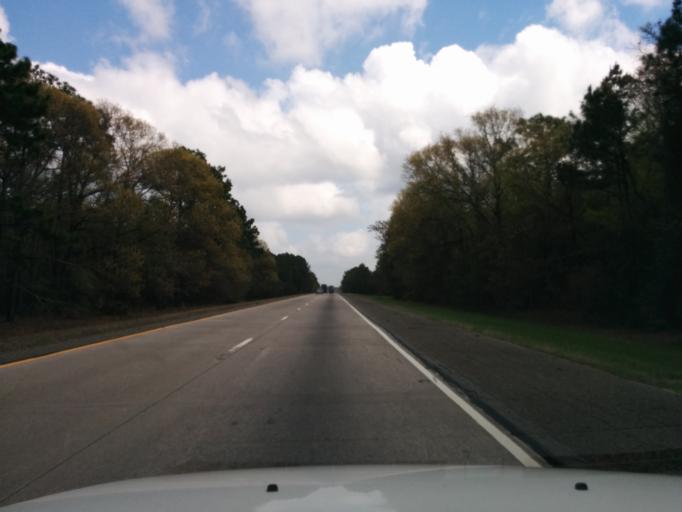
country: US
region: Georgia
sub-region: Bryan County
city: Pembroke
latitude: 32.2277
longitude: -81.5972
